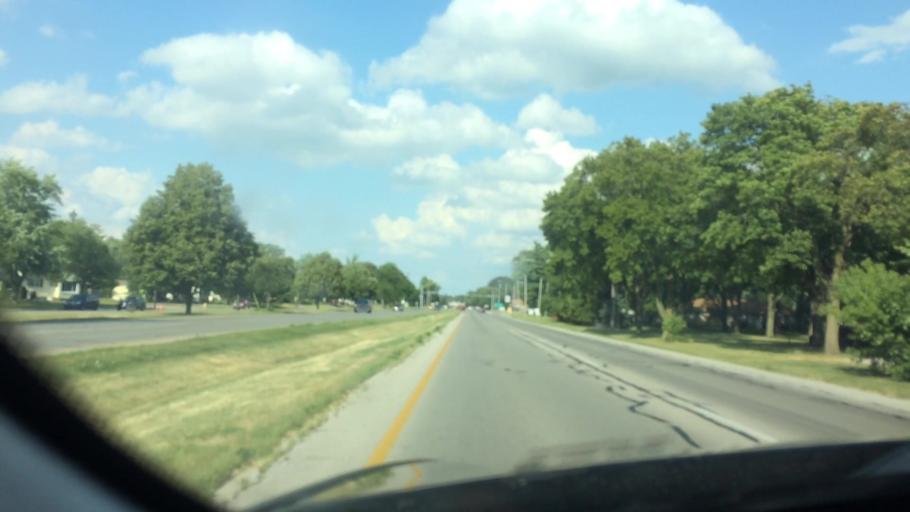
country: US
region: Ohio
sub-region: Wood County
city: Perrysburg
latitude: 41.5758
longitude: -83.6346
